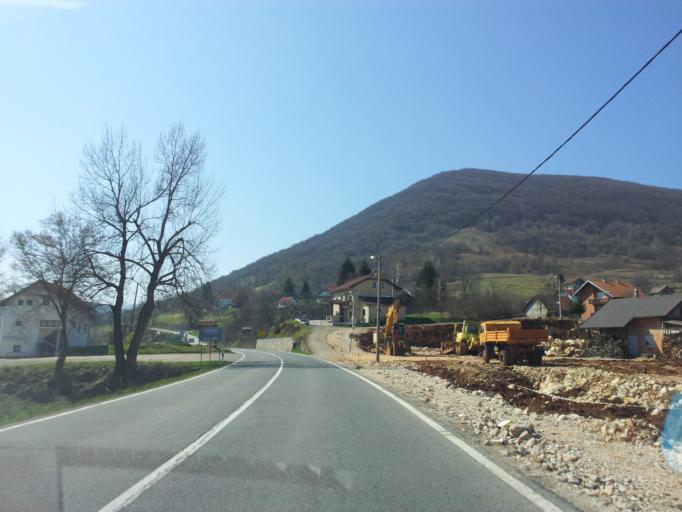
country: HR
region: Licko-Senjska
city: Jezerce
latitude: 44.9397
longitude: 15.6296
